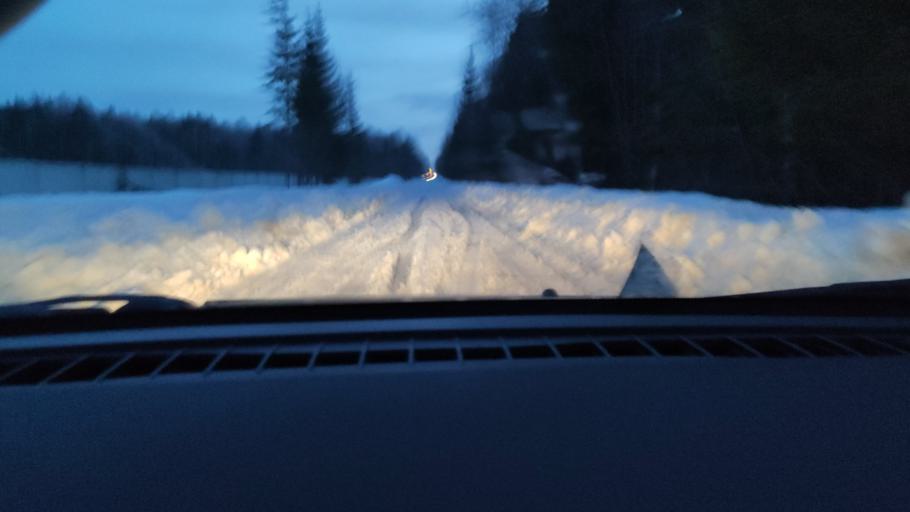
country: RU
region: Perm
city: Kondratovo
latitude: 58.0715
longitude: 56.1280
